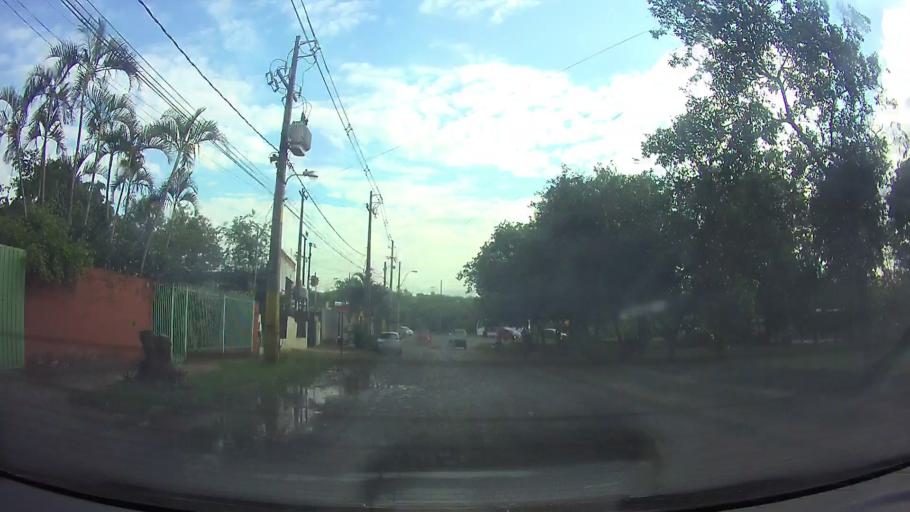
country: PY
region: Central
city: Fernando de la Mora
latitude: -25.2618
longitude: -57.5486
